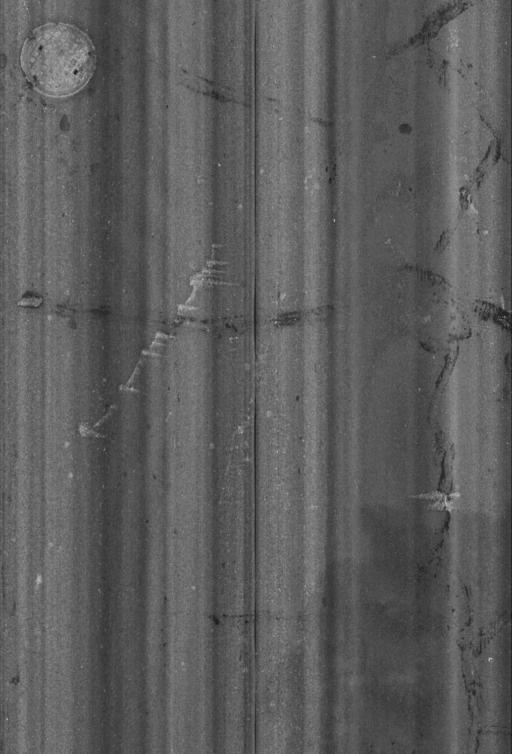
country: US
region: Maryland
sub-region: Prince George's County
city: Mount Rainier
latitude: 38.9367
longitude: -76.9701
